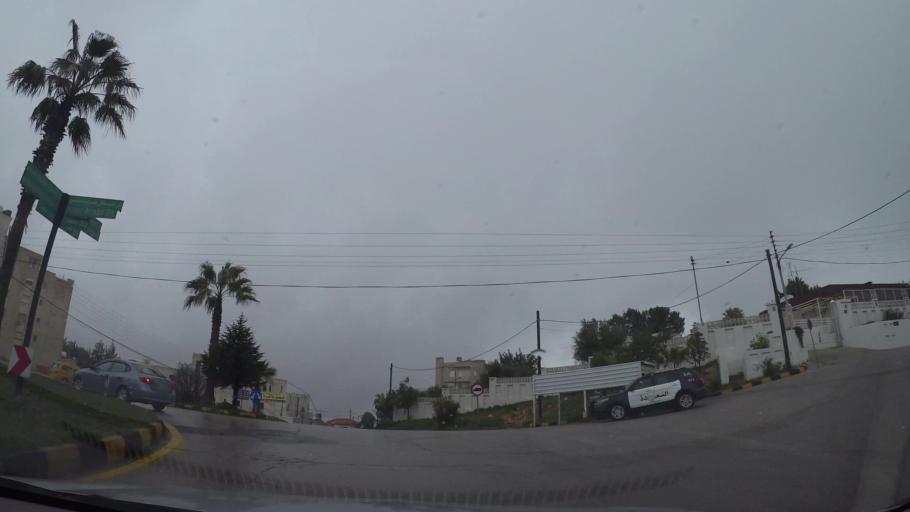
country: JO
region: Amman
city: Al Jubayhah
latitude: 32.0246
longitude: 35.8335
